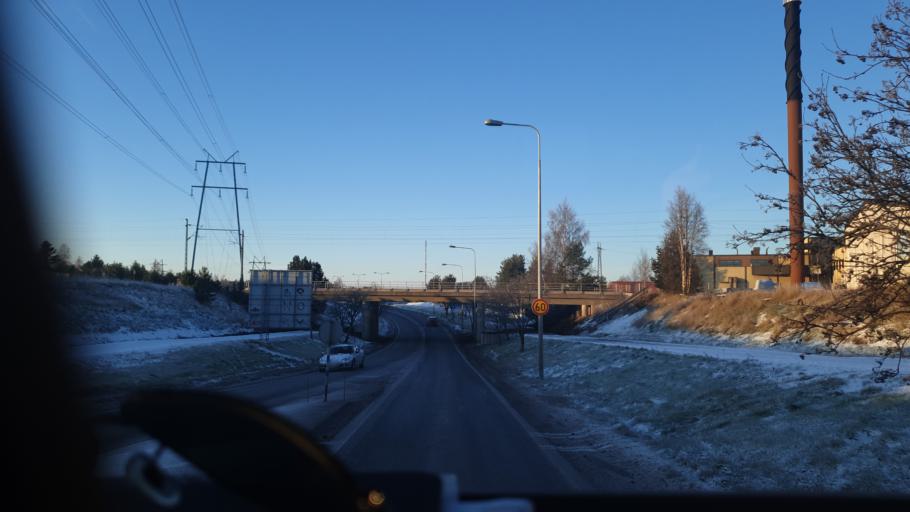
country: FI
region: Central Ostrobothnia
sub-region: Kokkola
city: Kokkola
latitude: 63.8311
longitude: 23.1177
